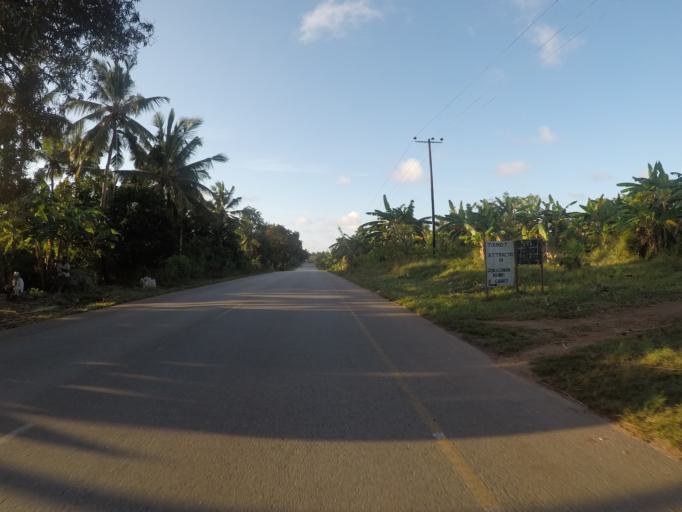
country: TZ
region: Zanzibar North
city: Kijini
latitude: -5.8294
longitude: 39.2916
